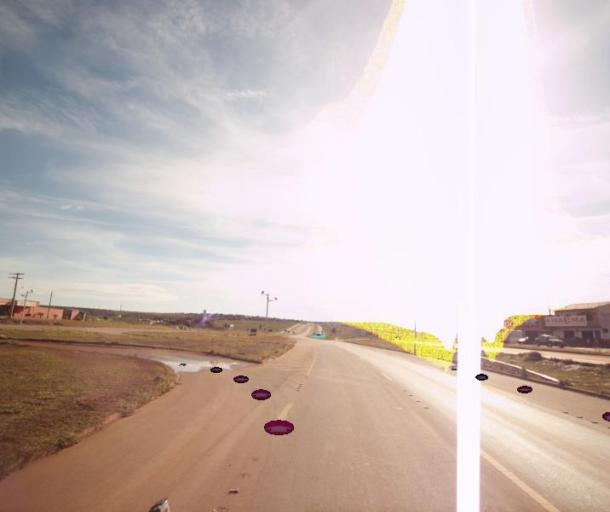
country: BR
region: Federal District
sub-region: Brasilia
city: Brasilia
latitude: -15.7522
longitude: -48.3257
